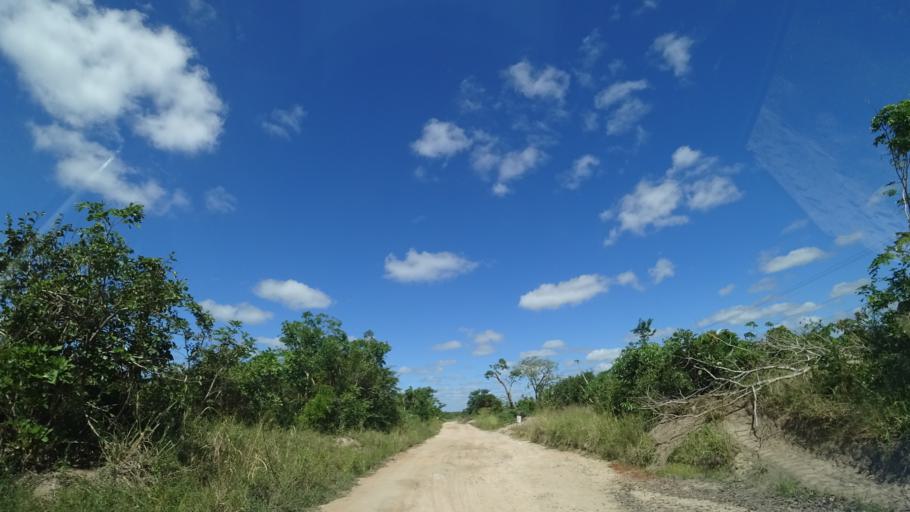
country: MZ
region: Sofala
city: Dondo
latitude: -19.2932
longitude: 34.6901
